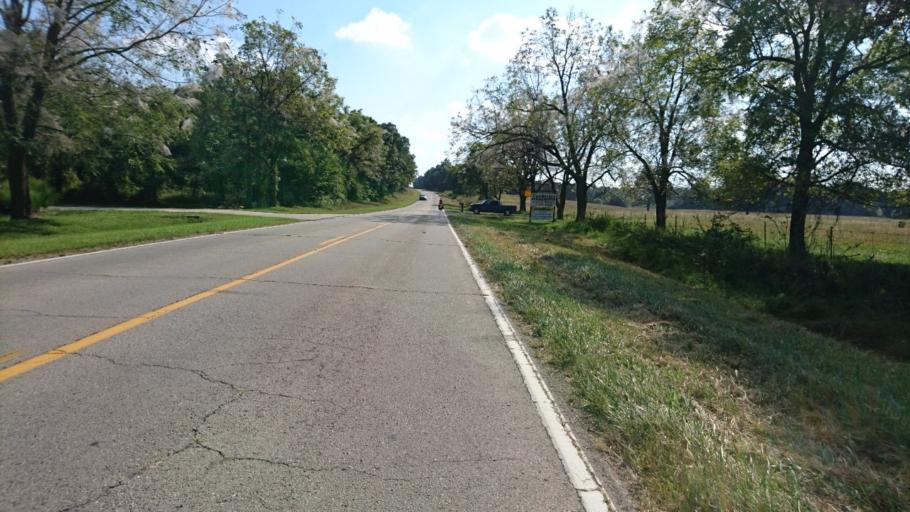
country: US
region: Missouri
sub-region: Laclede County
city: Lebanon
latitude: 37.6230
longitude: -92.6922
